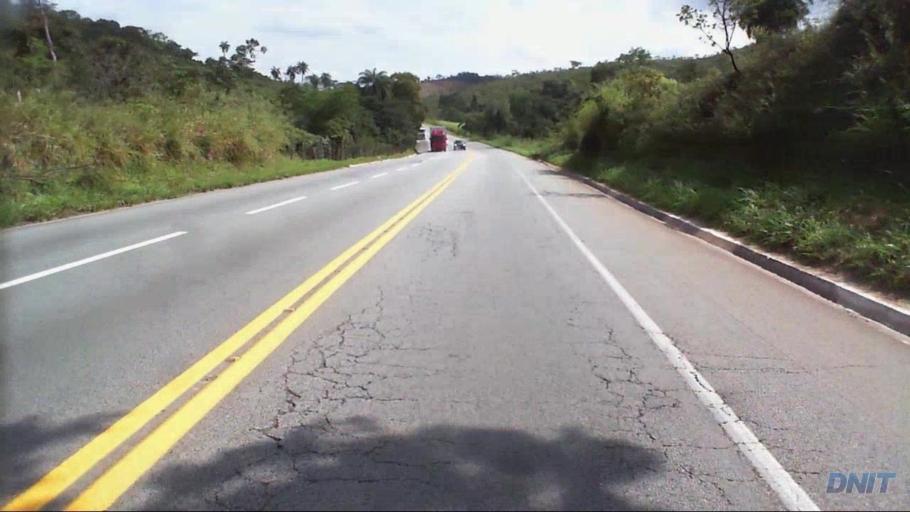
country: BR
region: Minas Gerais
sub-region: Santa Luzia
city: Santa Luzia
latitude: -19.8095
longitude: -43.7907
